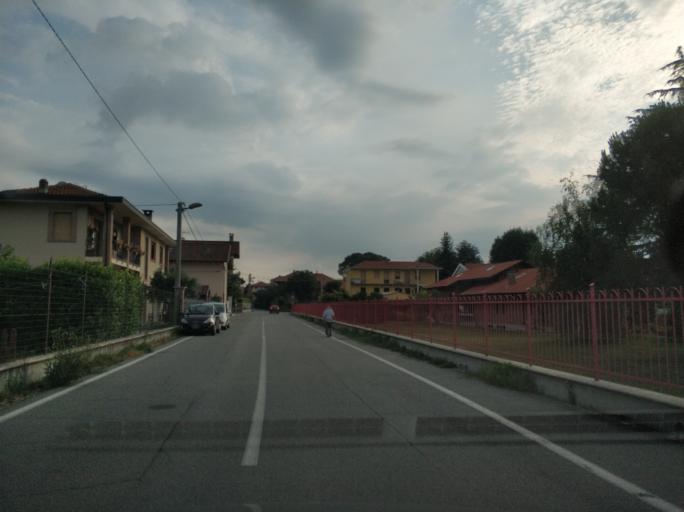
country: IT
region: Piedmont
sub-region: Provincia di Torino
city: Mathi
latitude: 45.2572
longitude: 7.5376
